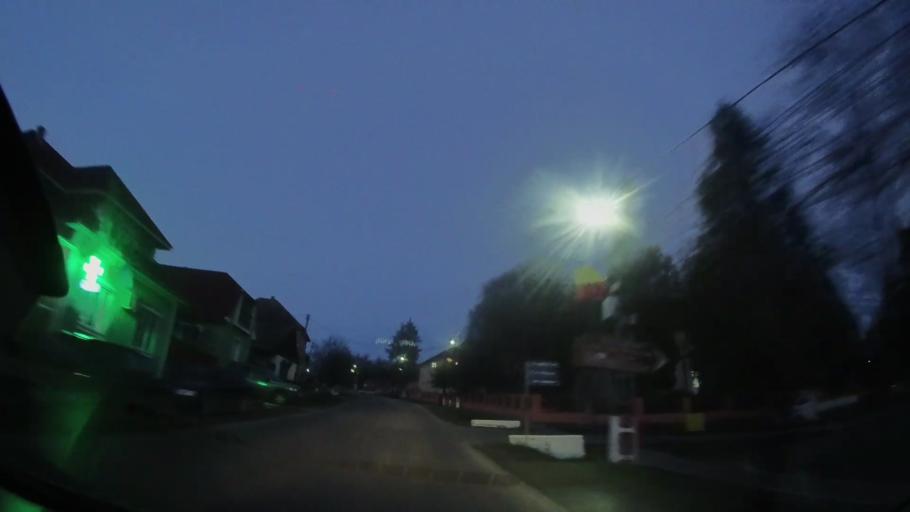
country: RO
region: Mures
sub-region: Comuna Sarmasu
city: Sarmasu
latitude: 46.7547
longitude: 24.1633
